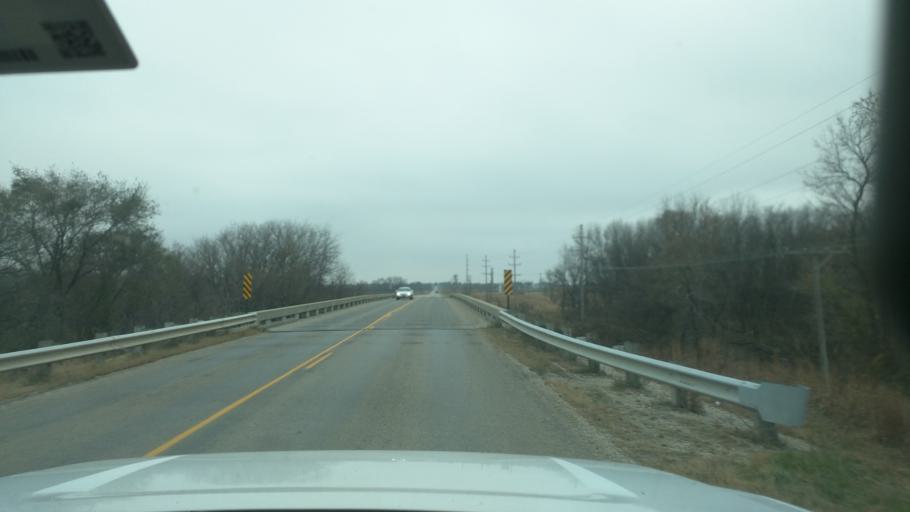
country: US
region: Kansas
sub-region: Lyon County
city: Emporia
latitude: 38.4722
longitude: -96.2530
